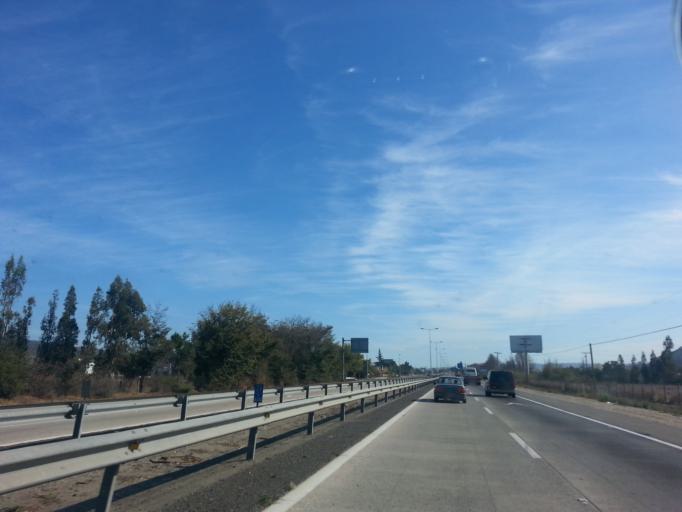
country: CL
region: Valparaiso
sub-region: Provincia de Marga Marga
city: Villa Alemana
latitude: -33.3355
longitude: -71.3775
